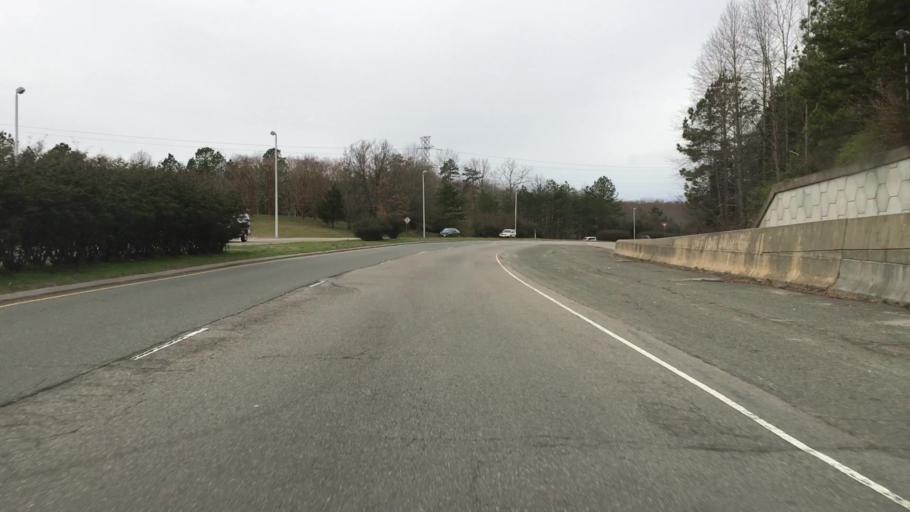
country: US
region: Virginia
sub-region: Chesterfield County
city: Bon Air
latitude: 37.5450
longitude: -77.5543
